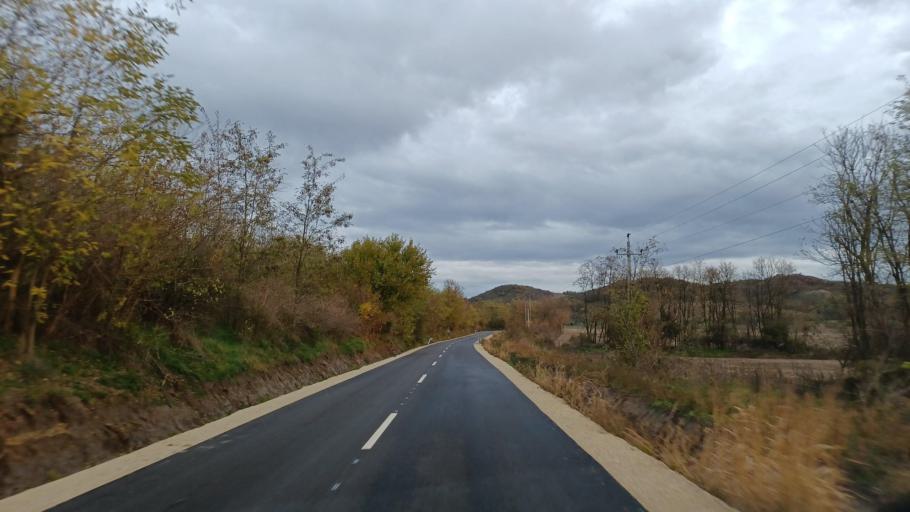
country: HU
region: Tolna
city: Gyonk
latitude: 46.5869
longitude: 18.4366
